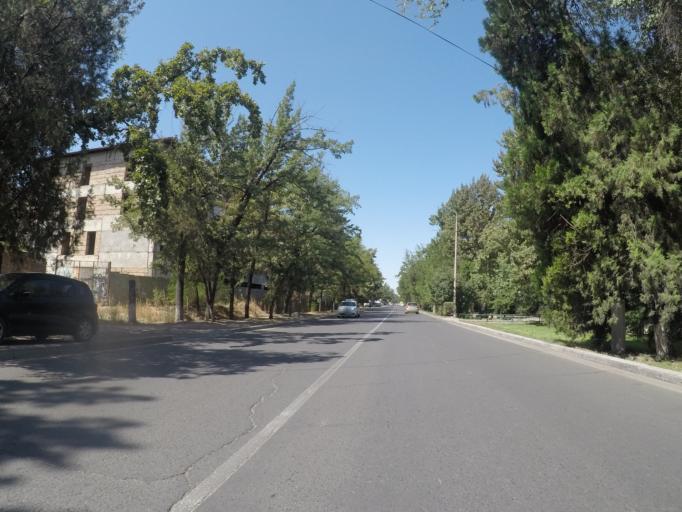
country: KG
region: Chuy
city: Bishkek
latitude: 42.8812
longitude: 74.5951
